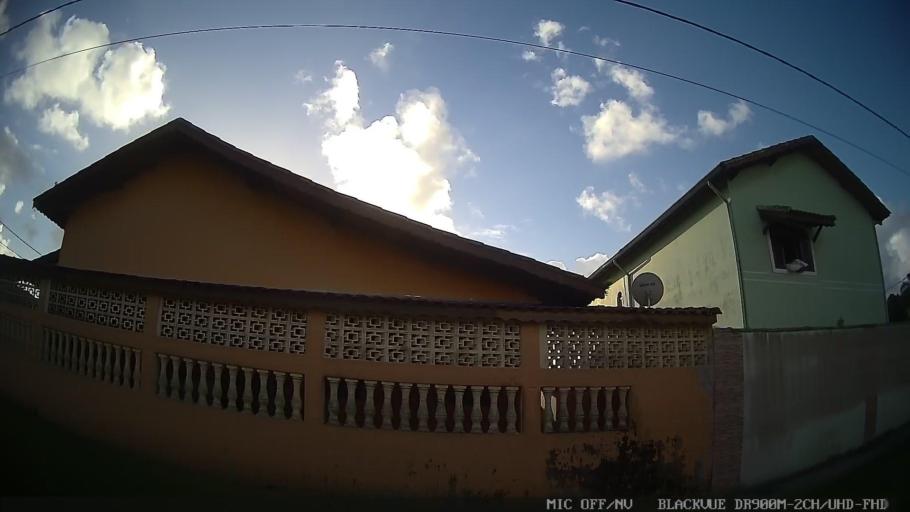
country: BR
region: Sao Paulo
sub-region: Itanhaem
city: Itanhaem
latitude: -24.1380
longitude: -46.7215
